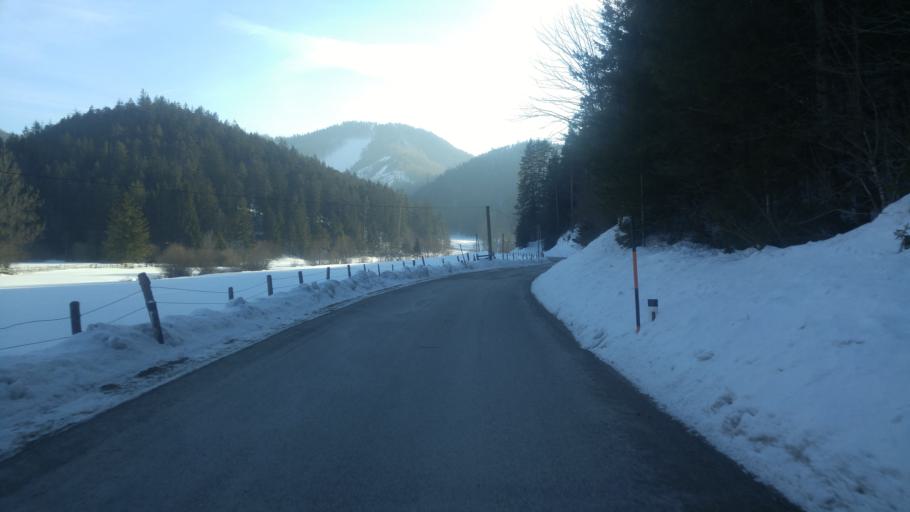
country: AT
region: Lower Austria
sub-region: Politischer Bezirk Lilienfeld
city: Hohenberg
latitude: 47.8919
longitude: 15.6188
